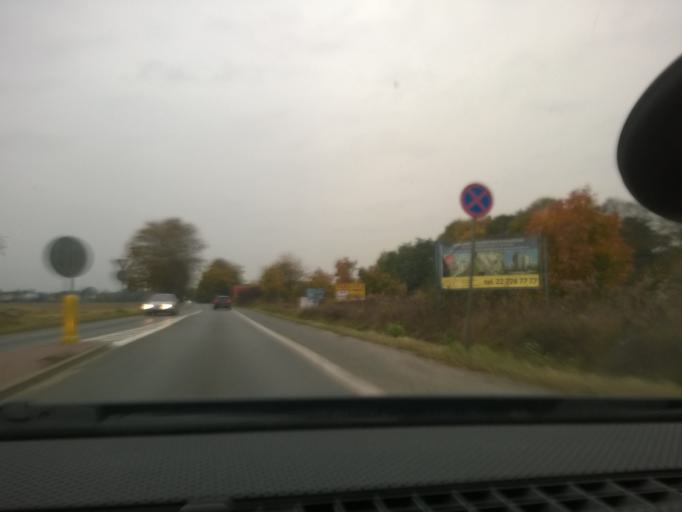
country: PL
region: Masovian Voivodeship
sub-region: Powiat pruszkowski
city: Komorow
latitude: 52.1567
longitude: 20.8344
